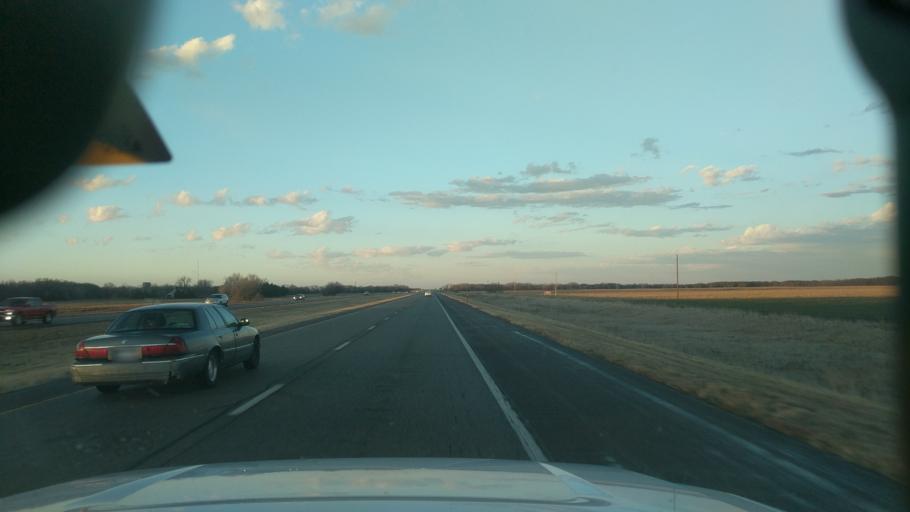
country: US
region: Kansas
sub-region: McPherson County
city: Lindsborg
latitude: 38.5966
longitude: -97.6211
